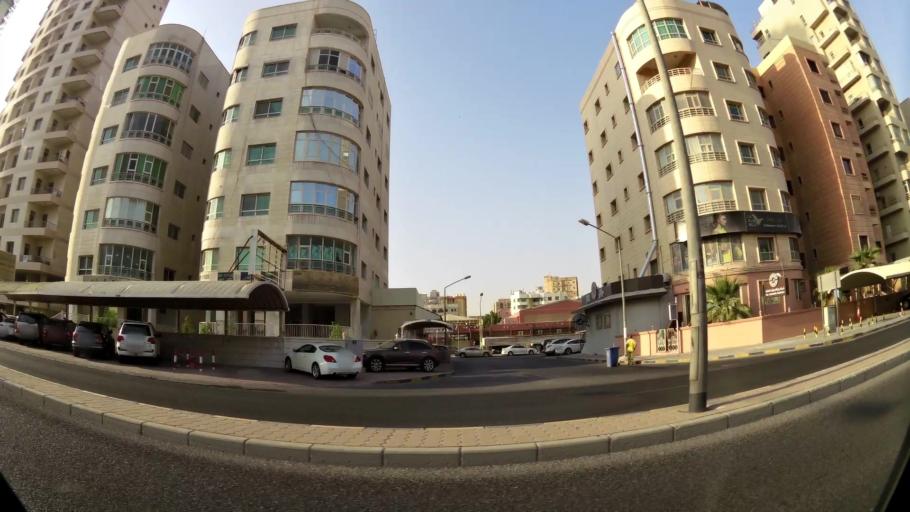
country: KW
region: Muhafazat Hawalli
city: Hawalli
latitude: 29.3400
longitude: 48.0434
